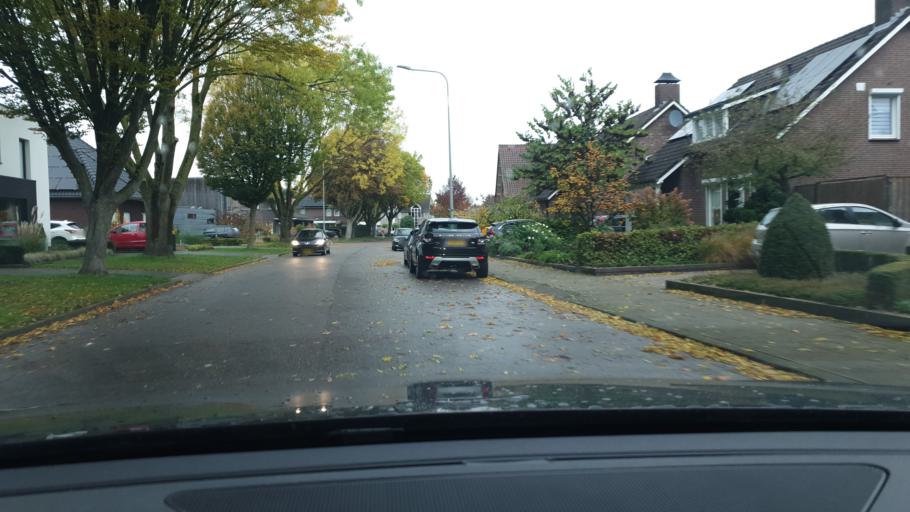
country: NL
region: Limburg
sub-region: Gemeente Peel en Maas
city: Maasbree
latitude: 51.4100
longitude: 6.0311
